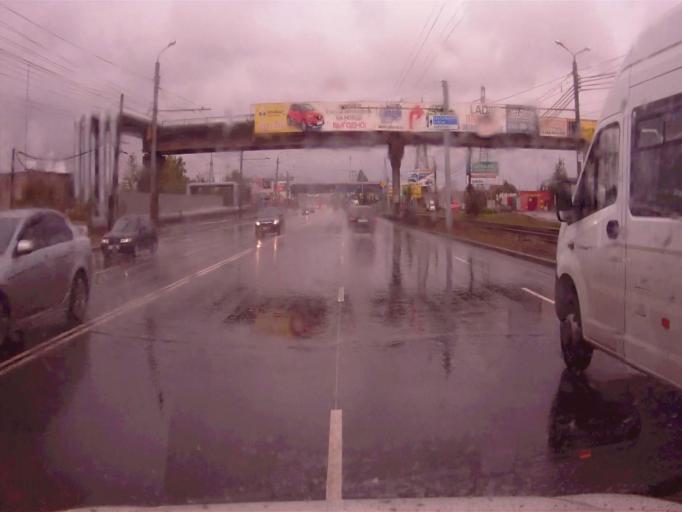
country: RU
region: Chelyabinsk
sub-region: Gorod Chelyabinsk
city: Chelyabinsk
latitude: 55.2030
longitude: 61.3854
